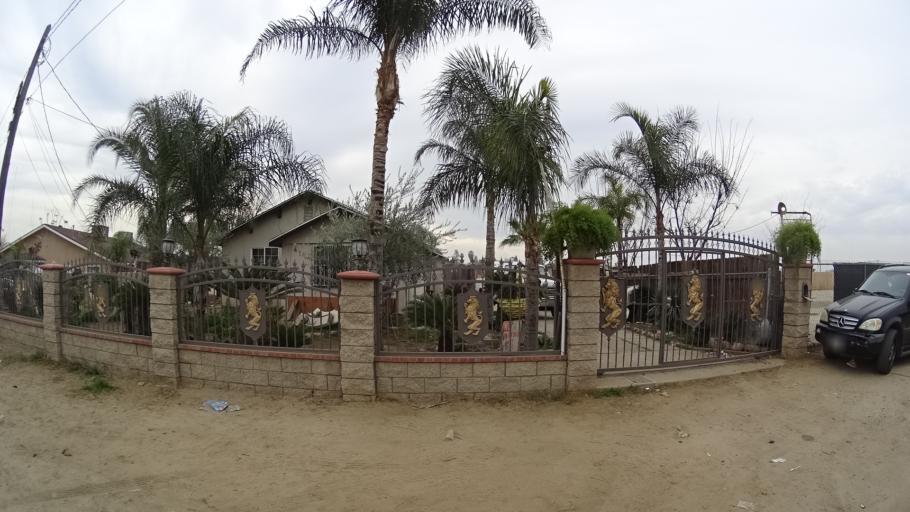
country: US
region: California
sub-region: Kern County
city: Bakersfield
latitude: 35.3499
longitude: -118.9966
